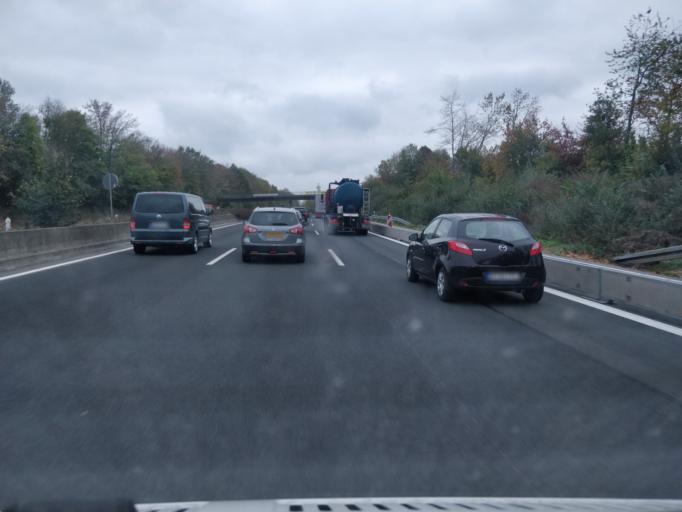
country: DE
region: North Rhine-Westphalia
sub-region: Regierungsbezirk Dusseldorf
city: Erkrath
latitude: 51.2640
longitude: 6.9148
